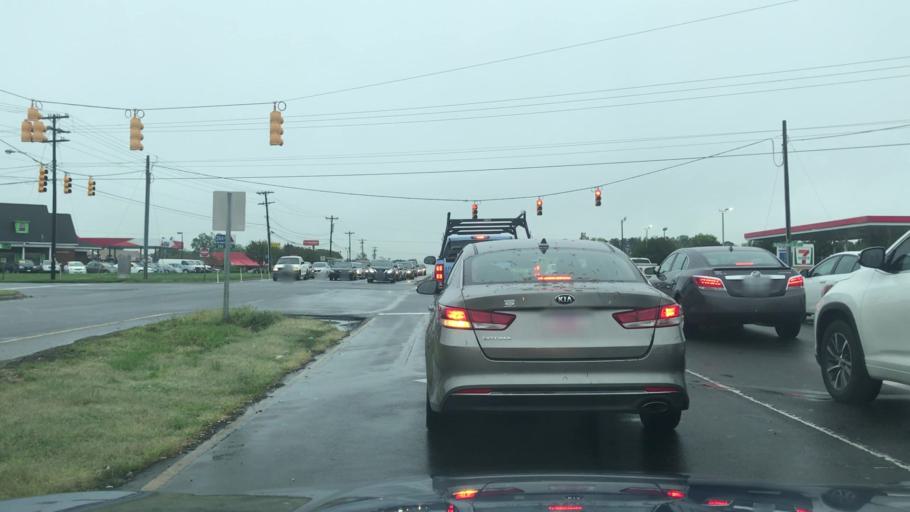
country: US
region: North Carolina
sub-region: Mecklenburg County
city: Matthews
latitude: 35.1192
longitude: -80.6983
